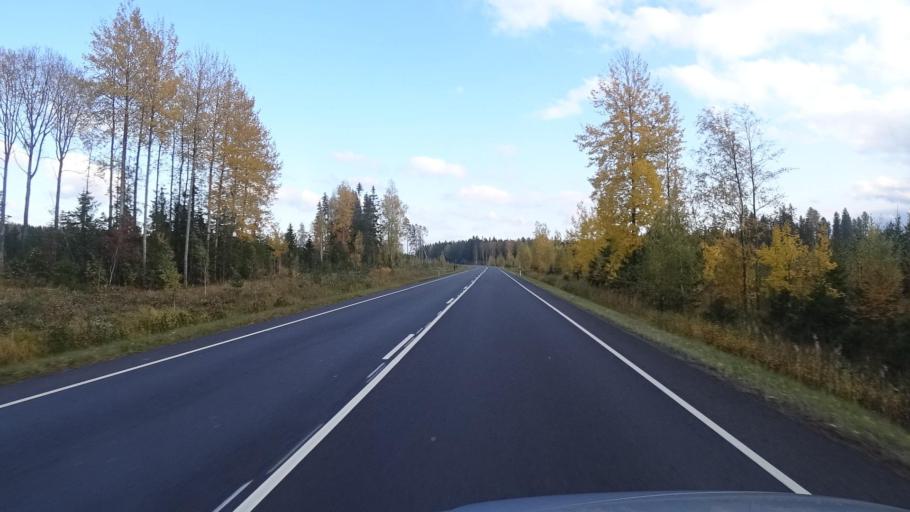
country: FI
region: Satakunta
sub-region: Rauma
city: Eura
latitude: 61.1097
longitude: 22.2099
